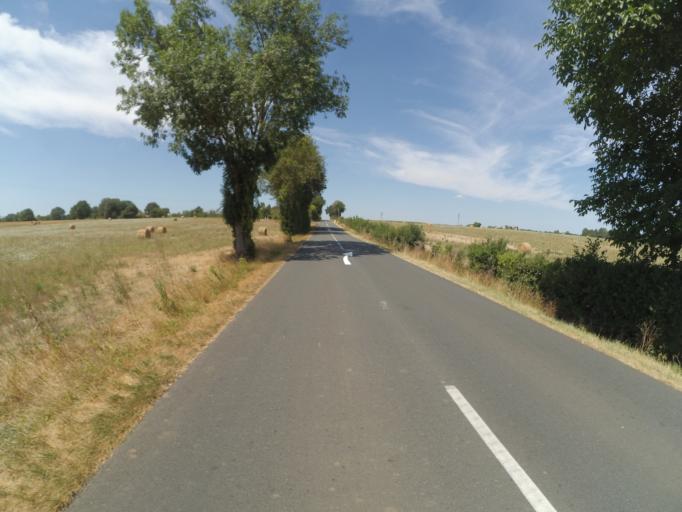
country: FR
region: Poitou-Charentes
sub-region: Departement de la Vienne
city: Usson-du-Poitou
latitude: 46.2871
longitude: 0.5127
